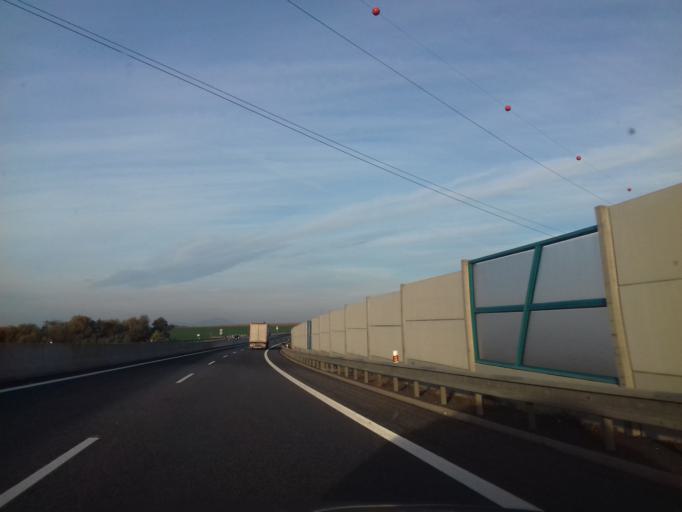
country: SK
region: Nitriansky
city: Zlate Moravce
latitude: 48.3516
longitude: 18.4724
